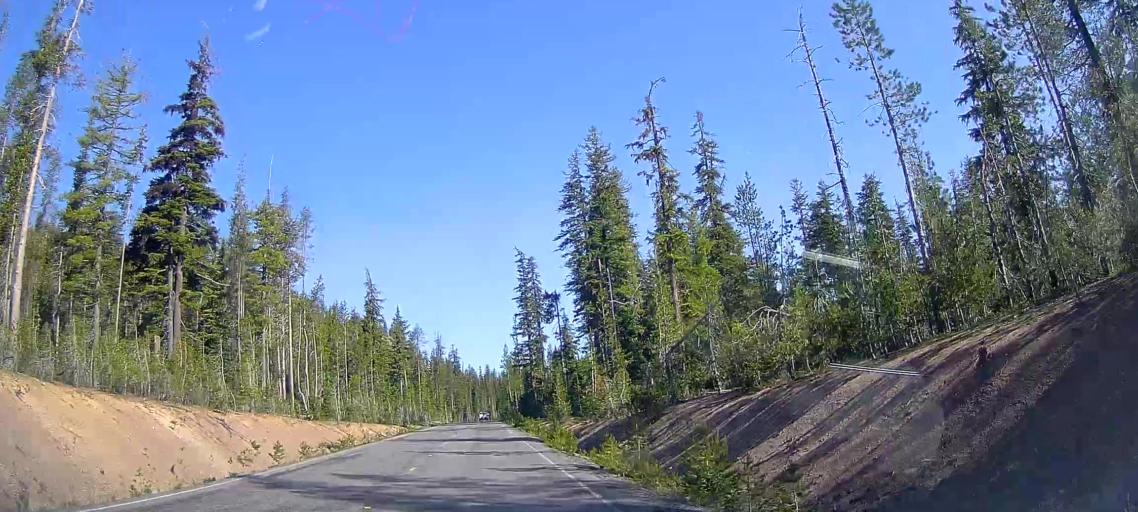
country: US
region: Oregon
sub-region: Jackson County
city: Shady Cove
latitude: 42.8510
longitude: -122.1496
